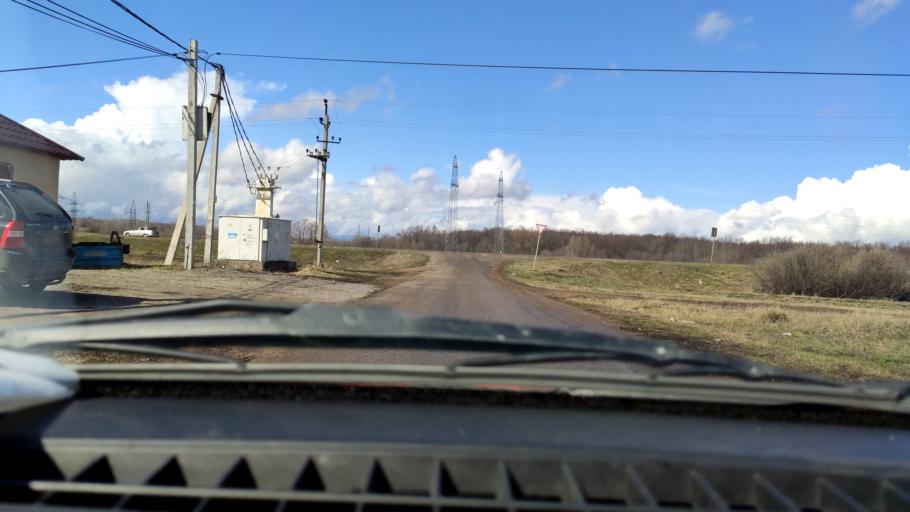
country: RU
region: Bashkortostan
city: Mikhaylovka
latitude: 54.8308
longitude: 55.9098
